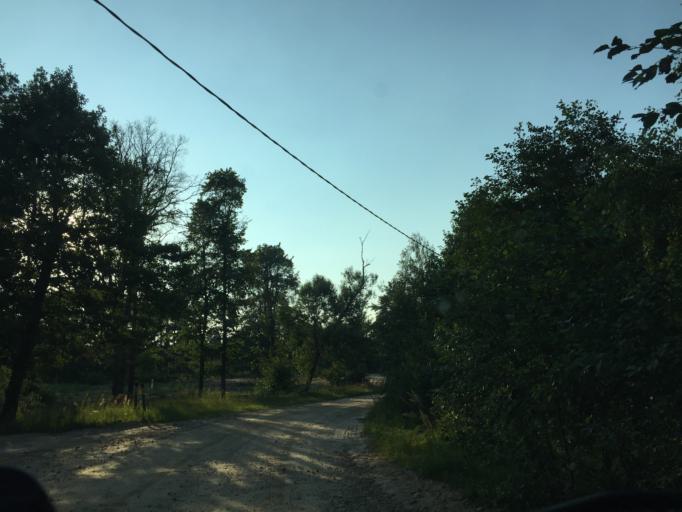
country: LV
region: Riga
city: Bergi
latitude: 56.9777
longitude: 24.3679
